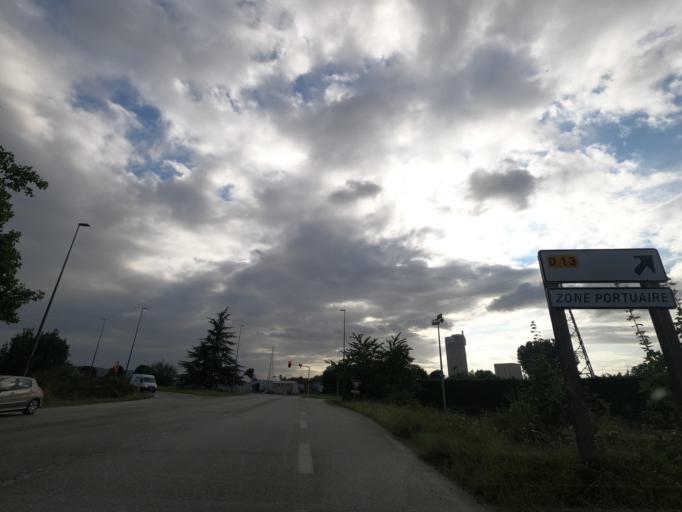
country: FR
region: Haute-Normandie
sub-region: Departement de la Seine-Maritime
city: Grand-Couronne
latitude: 49.3675
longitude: 1.0120
